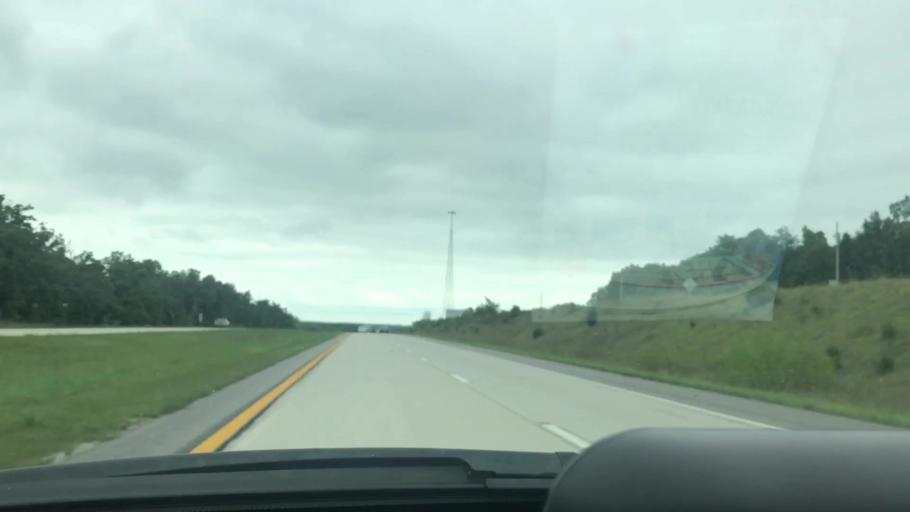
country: US
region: Missouri
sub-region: Greene County
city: Fair Grove
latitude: 37.5047
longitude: -93.1388
